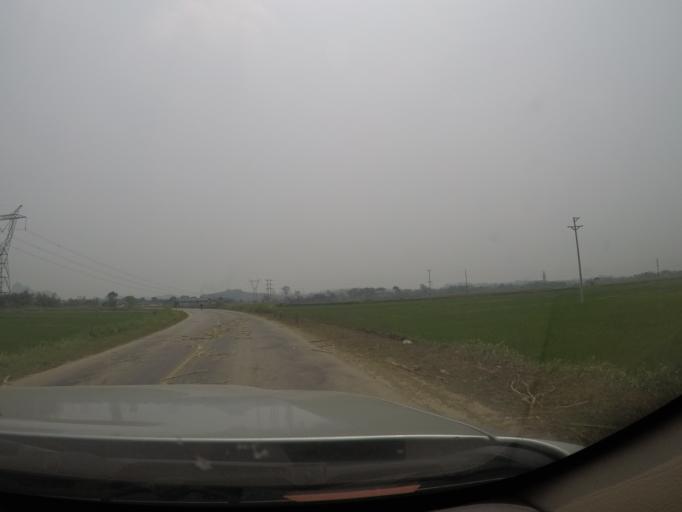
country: VN
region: Thanh Hoa
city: Thi Tran Thuong Xuan
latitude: 19.9154
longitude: 105.3949
